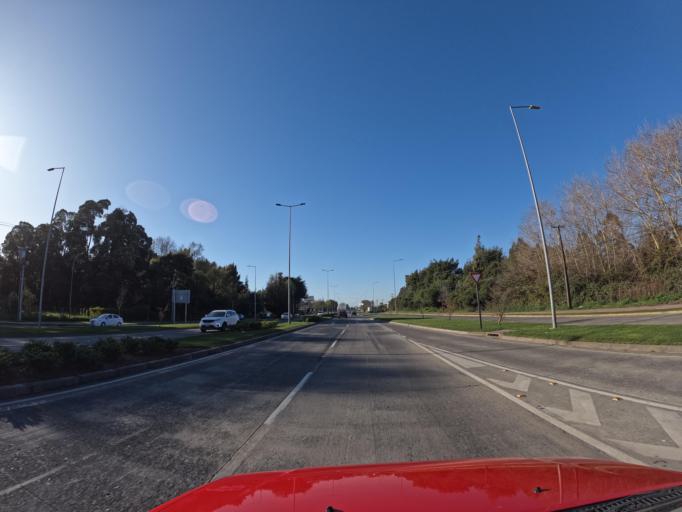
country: CL
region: Biobio
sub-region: Provincia de Concepcion
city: Concepcion
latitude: -36.7867
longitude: -73.0602
